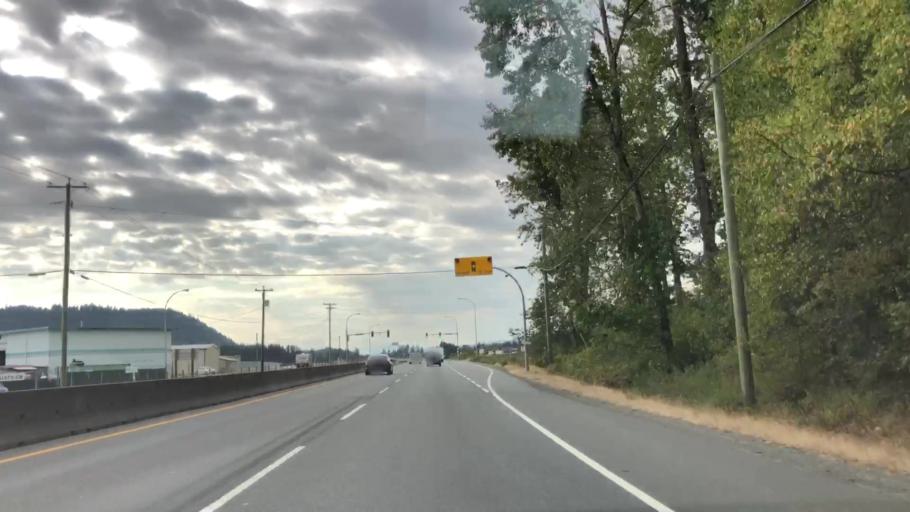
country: CA
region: British Columbia
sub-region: Cowichan Valley Regional District
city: Ladysmith
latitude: 49.0488
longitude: -123.8736
